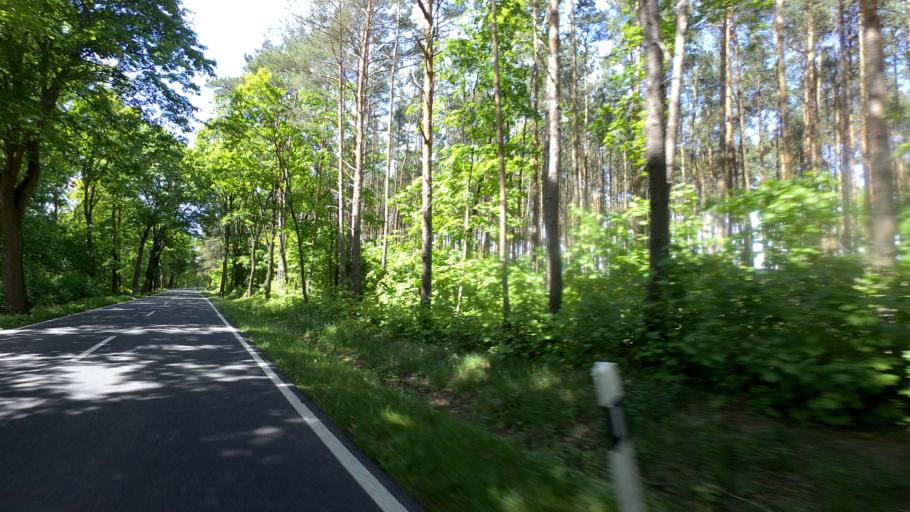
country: DE
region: Brandenburg
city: Baruth
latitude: 52.0656
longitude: 13.4772
